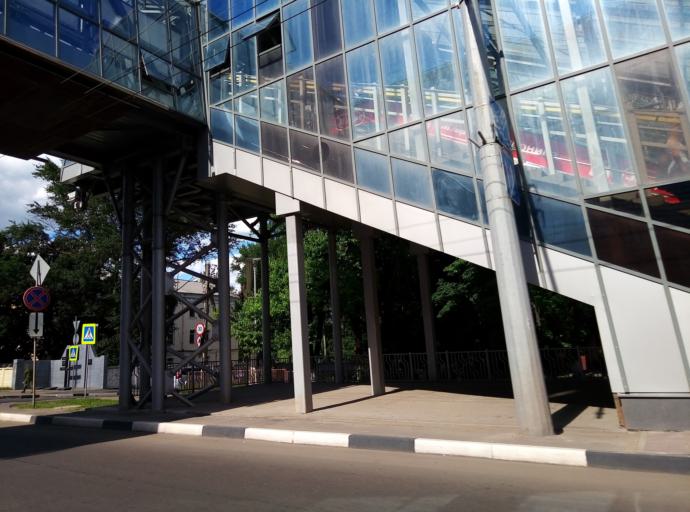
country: RU
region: Kursk
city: Kursk
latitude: 51.7619
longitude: 36.1857
